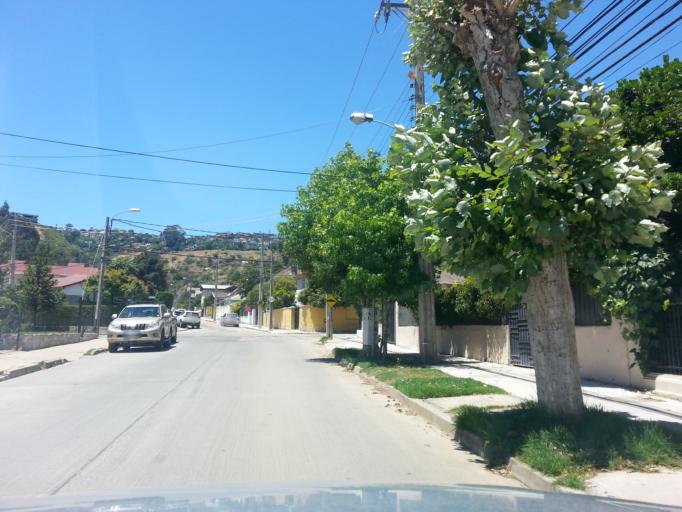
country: CL
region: Valparaiso
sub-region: Provincia de Valparaiso
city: Vina del Mar
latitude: -33.0333
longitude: -71.5251
